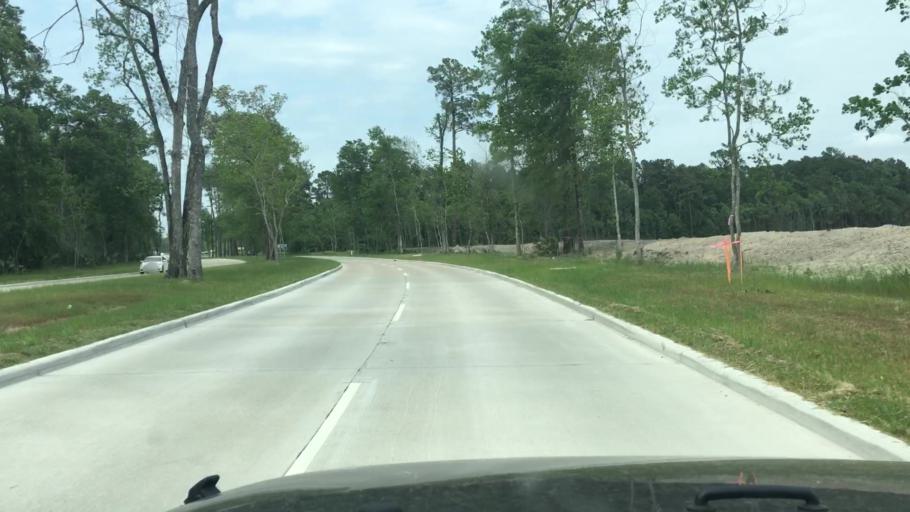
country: US
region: Texas
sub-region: Harris County
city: Atascocita
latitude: 29.9522
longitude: -95.2104
